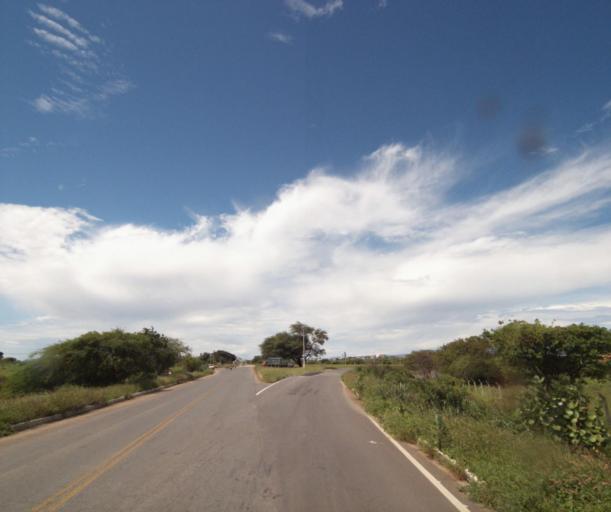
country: BR
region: Bahia
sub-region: Guanambi
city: Guanambi
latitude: -14.2483
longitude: -42.7817
